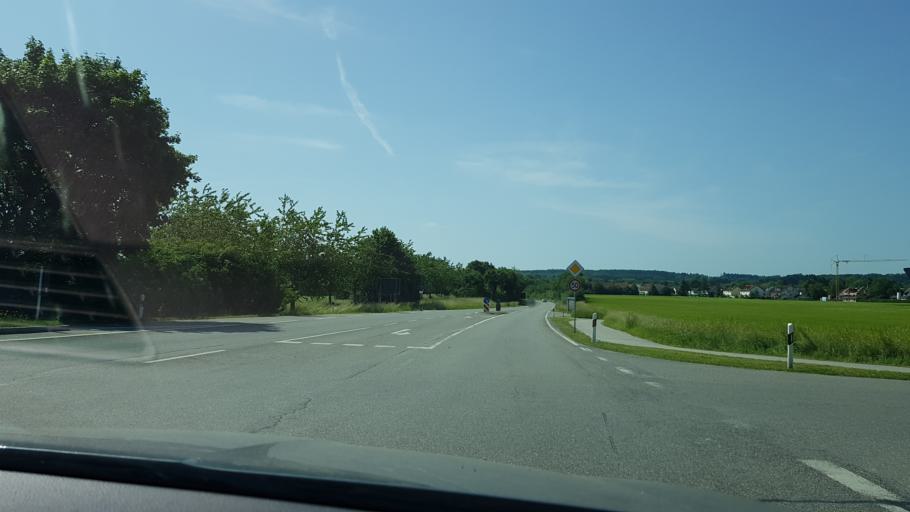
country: DE
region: Bavaria
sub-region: Upper Bavaria
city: Fuerstenfeldbruck
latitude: 48.1891
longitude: 11.2661
